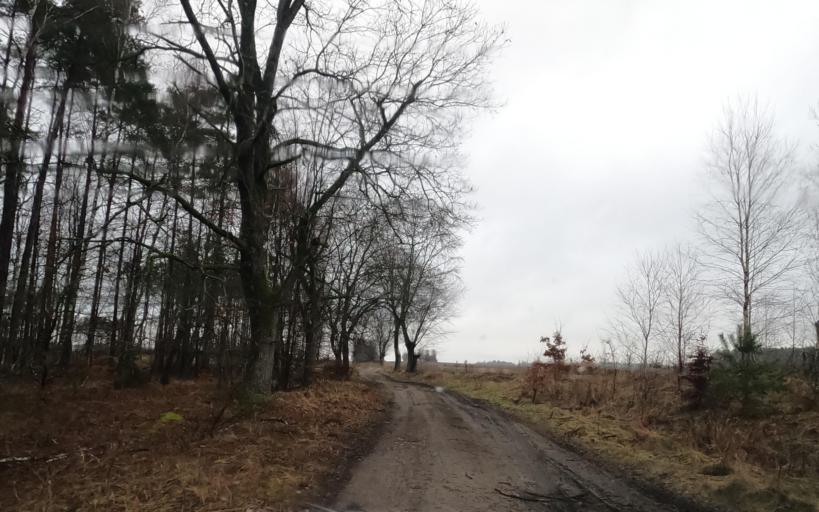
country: PL
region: West Pomeranian Voivodeship
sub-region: Powiat szczecinecki
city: Szczecinek
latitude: 53.6129
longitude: 16.6693
